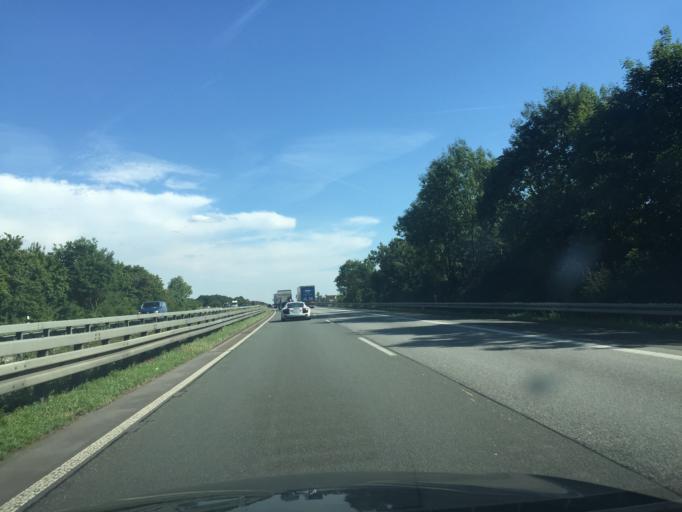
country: DE
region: Hesse
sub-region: Regierungsbezirk Giessen
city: Sinn
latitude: 50.6301
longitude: 8.3331
